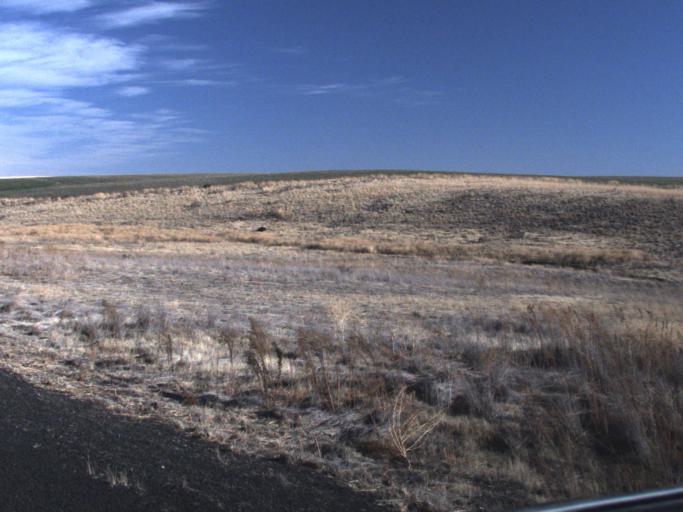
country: US
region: Washington
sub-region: Adams County
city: Ritzville
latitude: 47.1169
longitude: -118.6653
